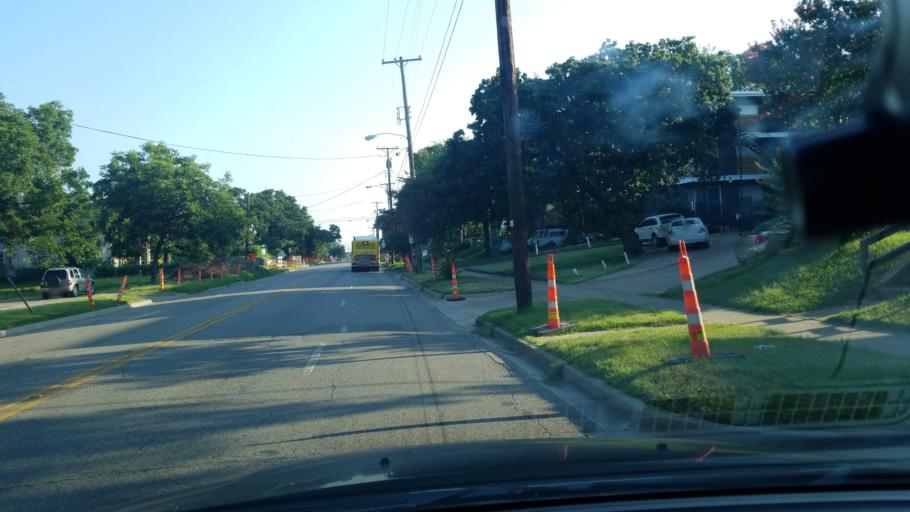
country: US
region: Texas
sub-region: Dallas County
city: Dallas
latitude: 32.7550
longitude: -96.8156
